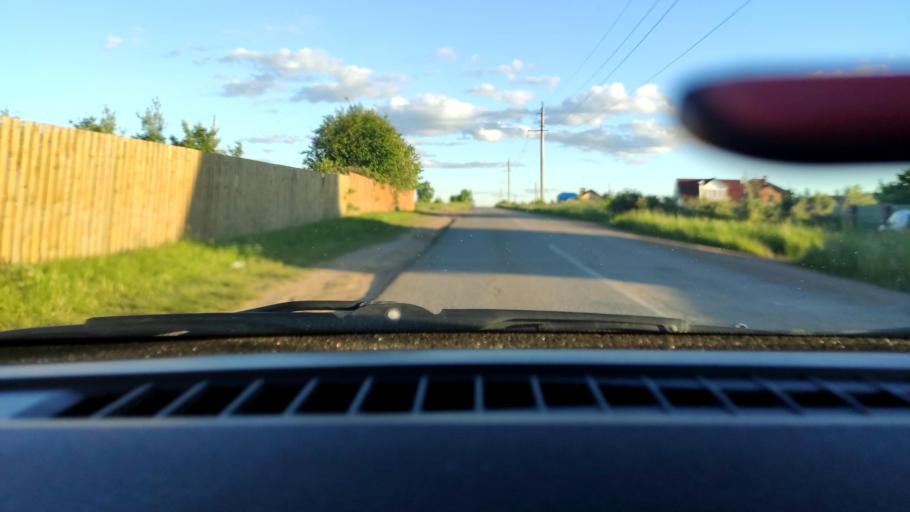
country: RU
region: Perm
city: Kultayevo
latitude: 57.9352
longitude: 55.8647
